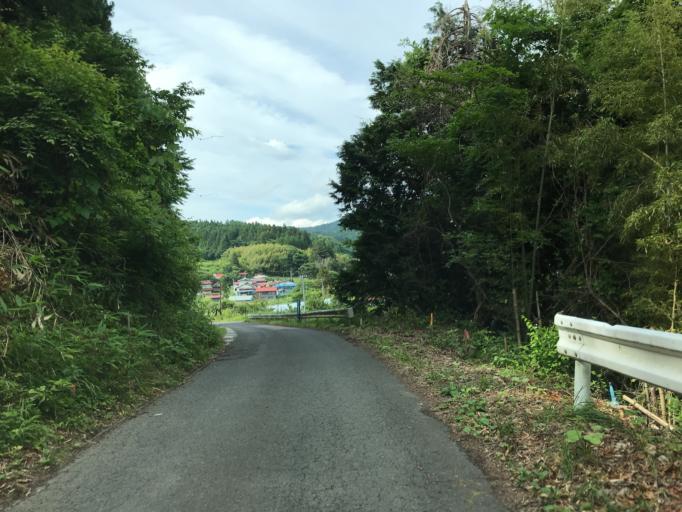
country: JP
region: Fukushima
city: Funehikimachi-funehiki
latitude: 37.5114
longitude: 140.6497
